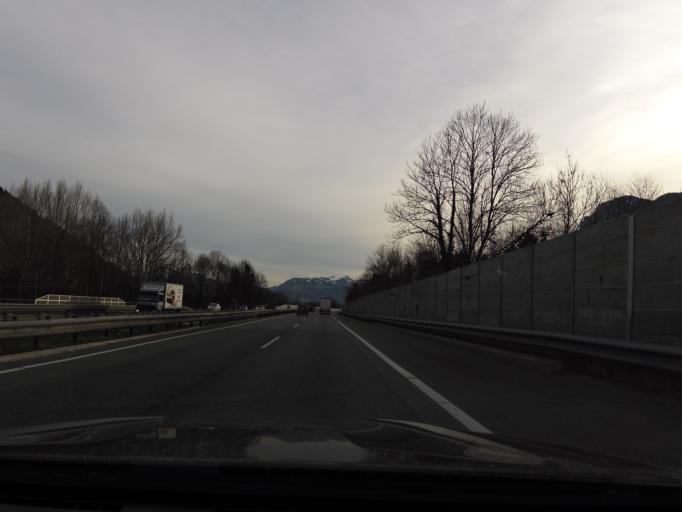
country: AT
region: Tyrol
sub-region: Politischer Bezirk Kufstein
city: Kufstein
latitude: 47.5965
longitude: 12.1757
